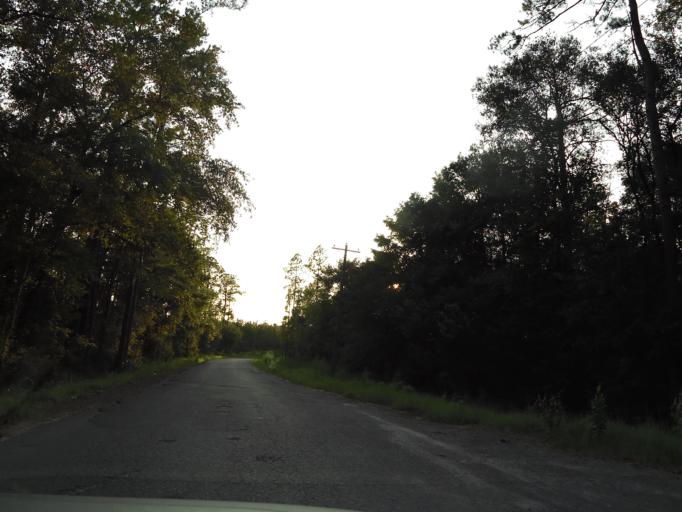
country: US
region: Florida
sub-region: Duval County
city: Baldwin
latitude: 30.3842
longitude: -82.0400
